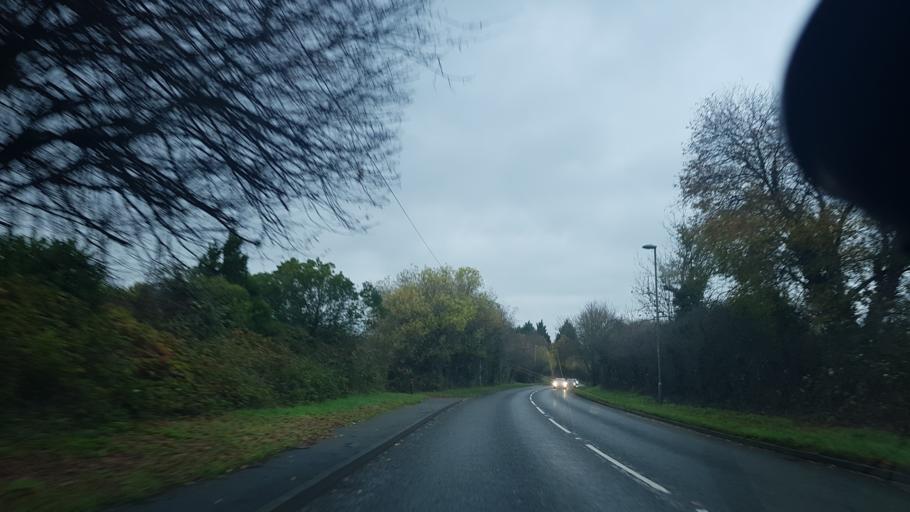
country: GB
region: England
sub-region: Surrey
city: Chilworth
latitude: 51.2493
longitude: -0.5261
